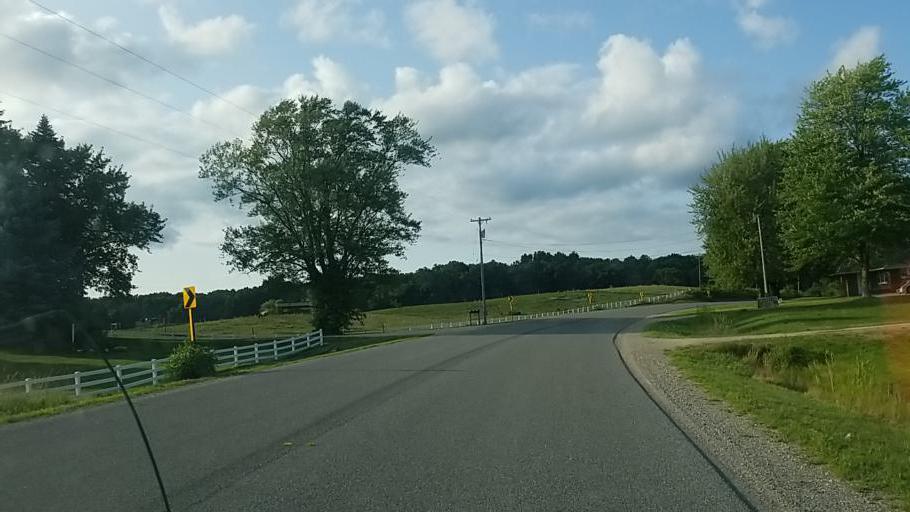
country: US
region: Michigan
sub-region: Kent County
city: Lowell
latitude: 43.0513
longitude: -85.3546
